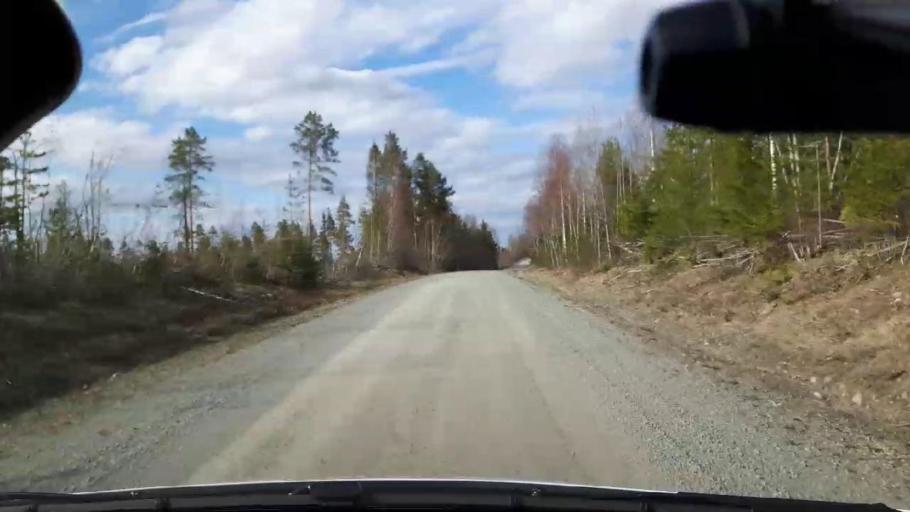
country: SE
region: Jaemtland
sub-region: Bergs Kommun
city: Hoverberg
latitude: 62.7528
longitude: 14.6624
